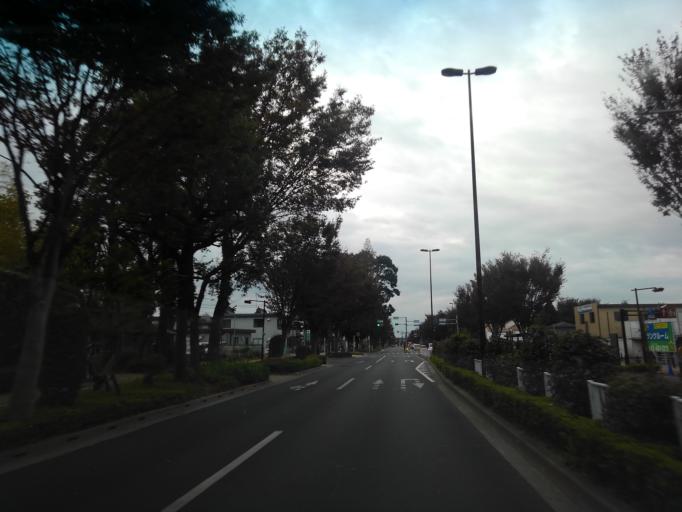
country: JP
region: Tokyo
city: Mitaka-shi
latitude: 35.6774
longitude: 139.5468
